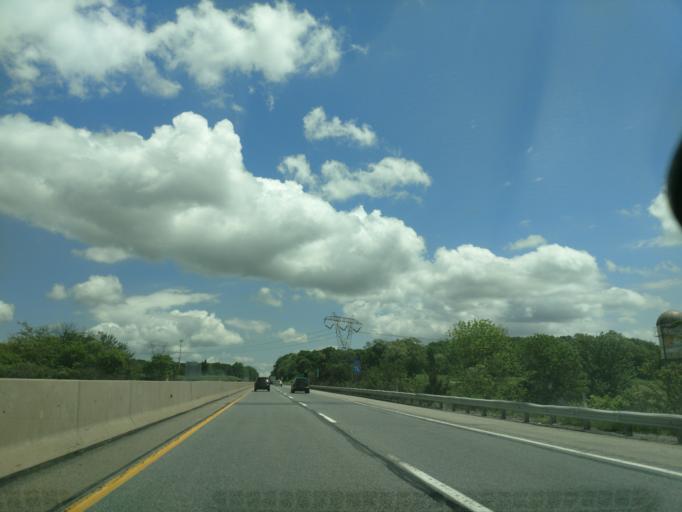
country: US
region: Pennsylvania
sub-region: Lancaster County
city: Swartzville
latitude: 40.2152
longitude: -76.0690
